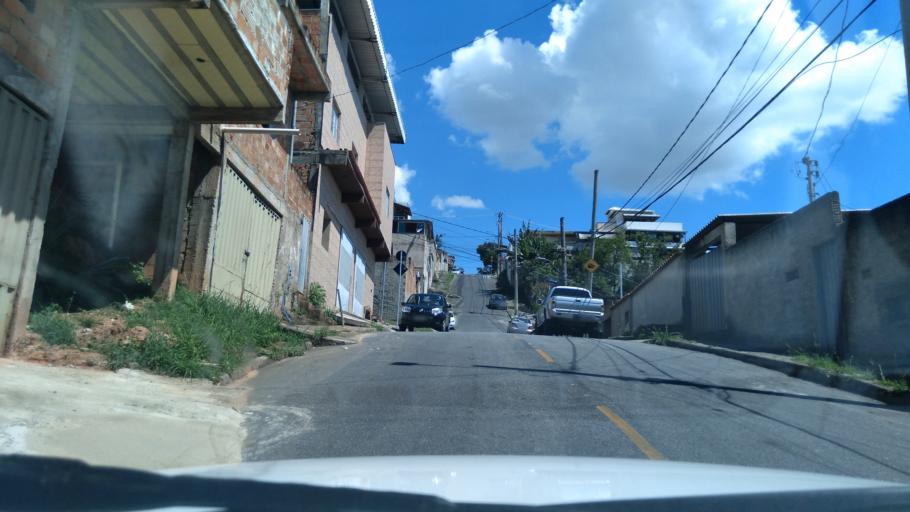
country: BR
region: Minas Gerais
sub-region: Belo Horizonte
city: Belo Horizonte
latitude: -19.8753
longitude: -43.9131
